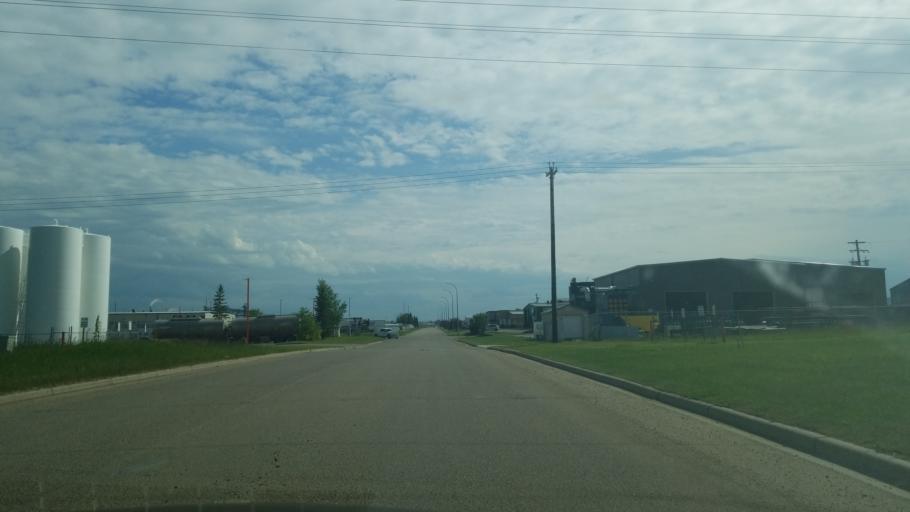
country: CA
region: Saskatchewan
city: Lloydminster
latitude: 53.2928
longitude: -110.0368
